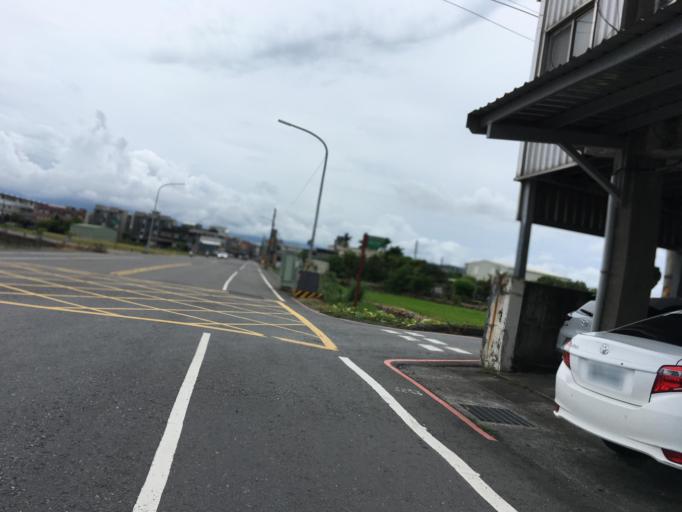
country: TW
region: Taiwan
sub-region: Yilan
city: Yilan
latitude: 24.6879
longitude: 121.8032
